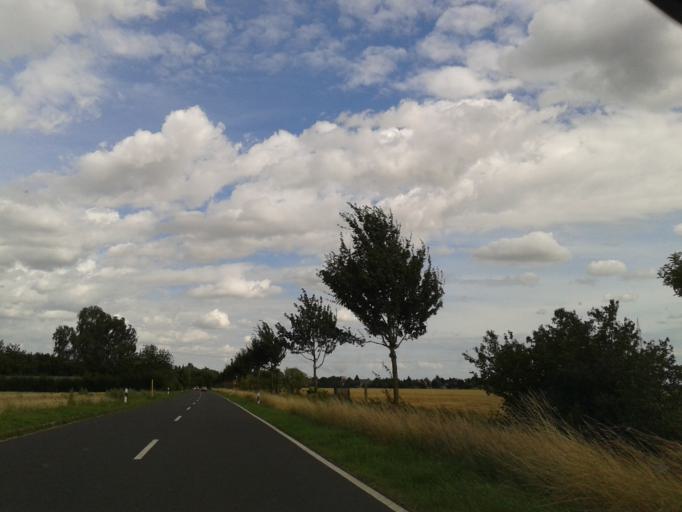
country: DE
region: Saxony-Anhalt
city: Halle (Saale)
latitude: 51.5124
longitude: 12.0217
